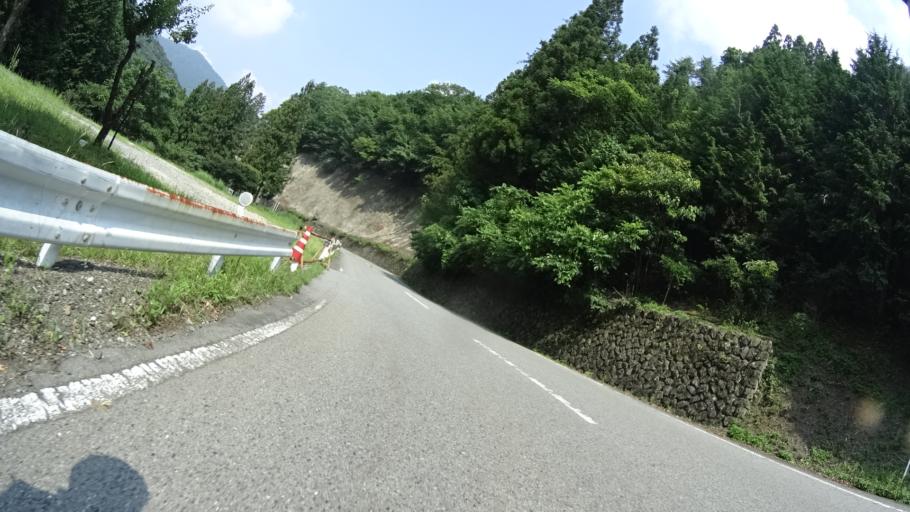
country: JP
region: Gunma
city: Tomioka
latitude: 36.0609
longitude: 138.8405
